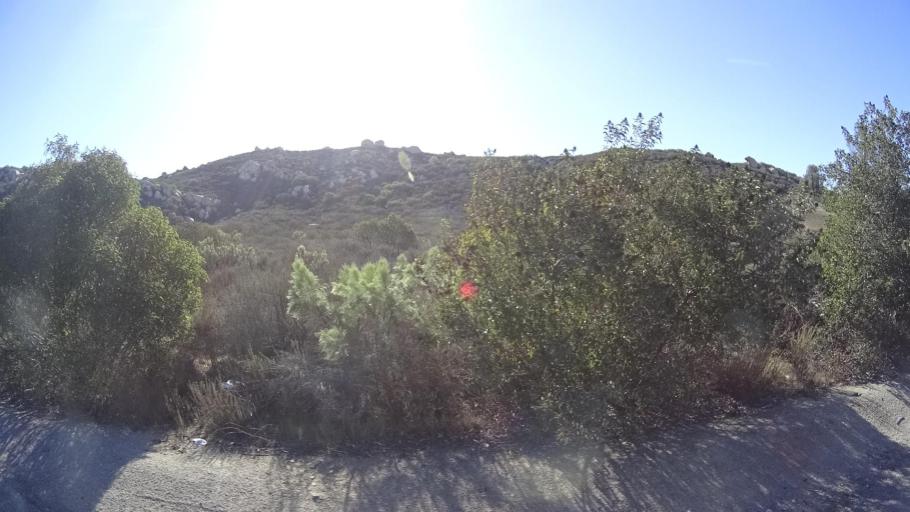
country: US
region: California
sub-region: San Diego County
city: Jamul
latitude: 32.6665
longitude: -116.7863
